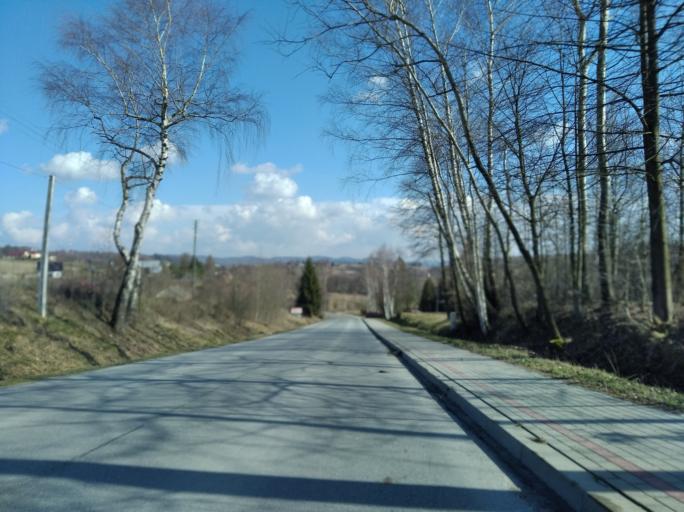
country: PL
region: Subcarpathian Voivodeship
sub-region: Powiat strzyzowski
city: Frysztak
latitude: 49.8447
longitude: 21.5694
